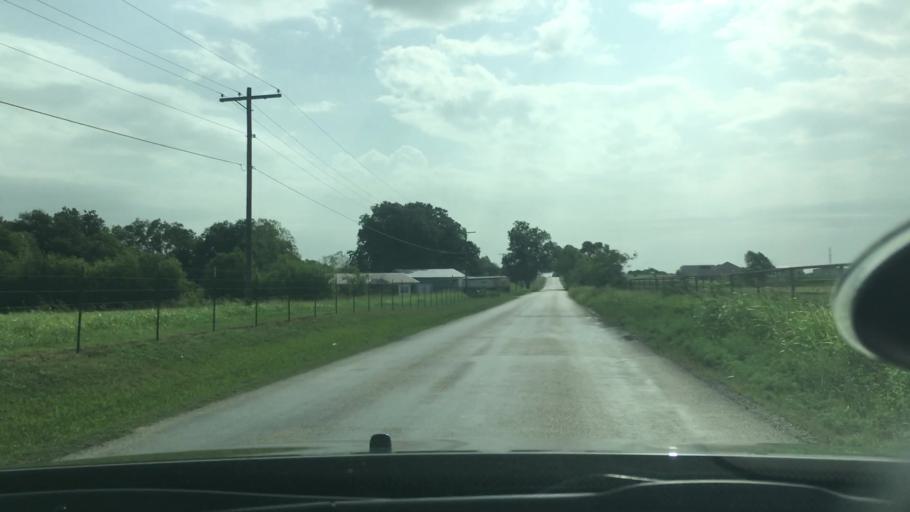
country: US
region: Oklahoma
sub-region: Carter County
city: Lone Grove
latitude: 34.2020
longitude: -97.2552
